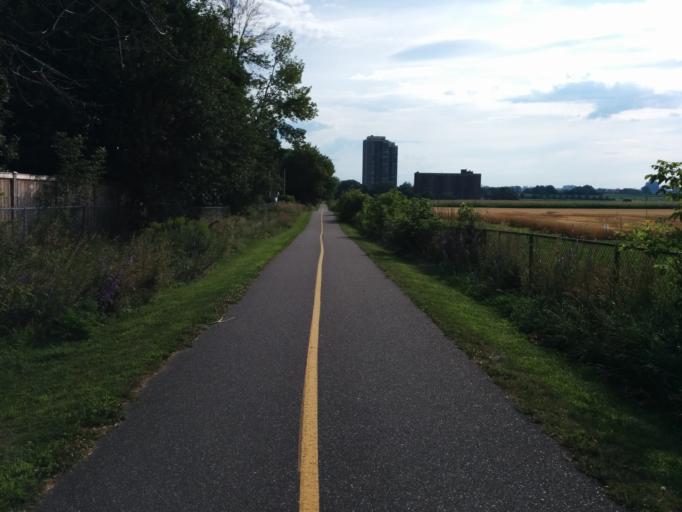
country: CA
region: Ontario
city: Ottawa
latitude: 45.3748
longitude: -75.7293
